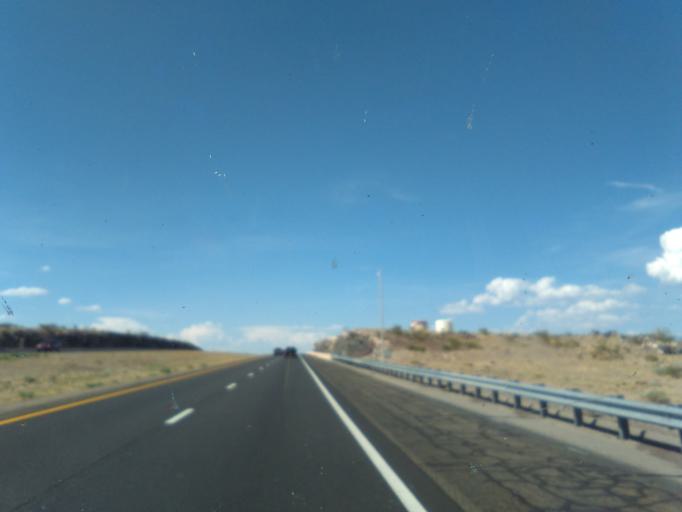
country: US
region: New Mexico
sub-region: Valencia County
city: Bosque Farms
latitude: 34.9137
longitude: -106.7216
